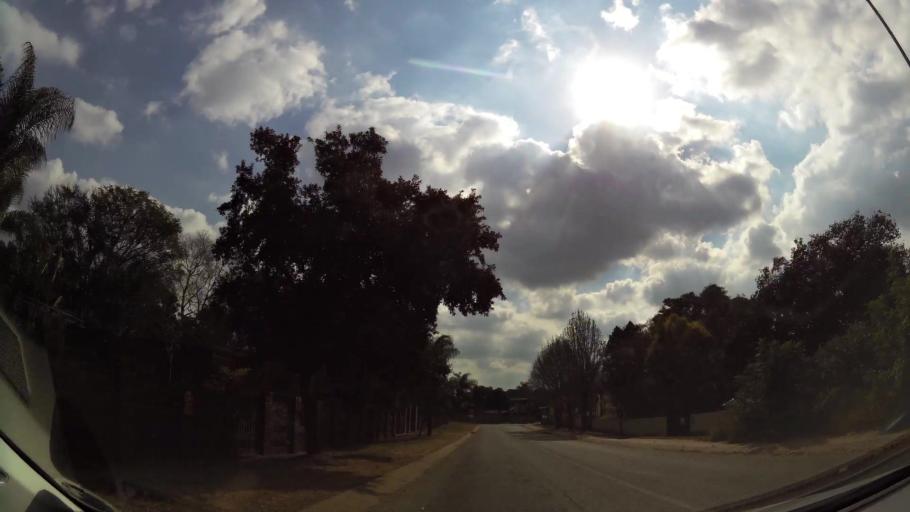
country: ZA
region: Gauteng
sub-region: City of Tshwane Metropolitan Municipality
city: Pretoria
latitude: -25.7525
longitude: 28.3132
